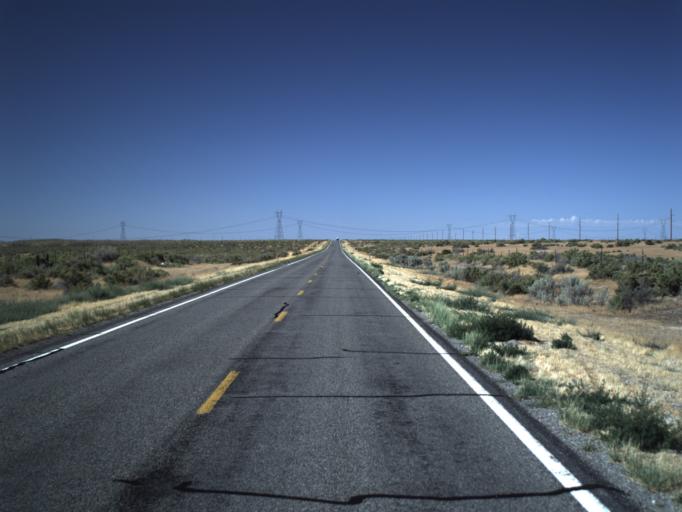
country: US
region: Utah
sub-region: Millard County
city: Delta
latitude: 39.5011
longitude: -112.3915
